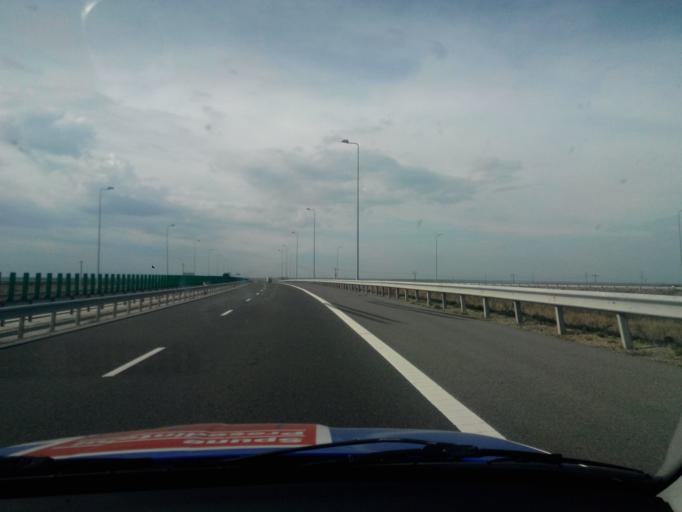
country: RO
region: Constanta
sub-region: Comuna Cumpana
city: Cumpana
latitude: 44.1451
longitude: 28.5508
